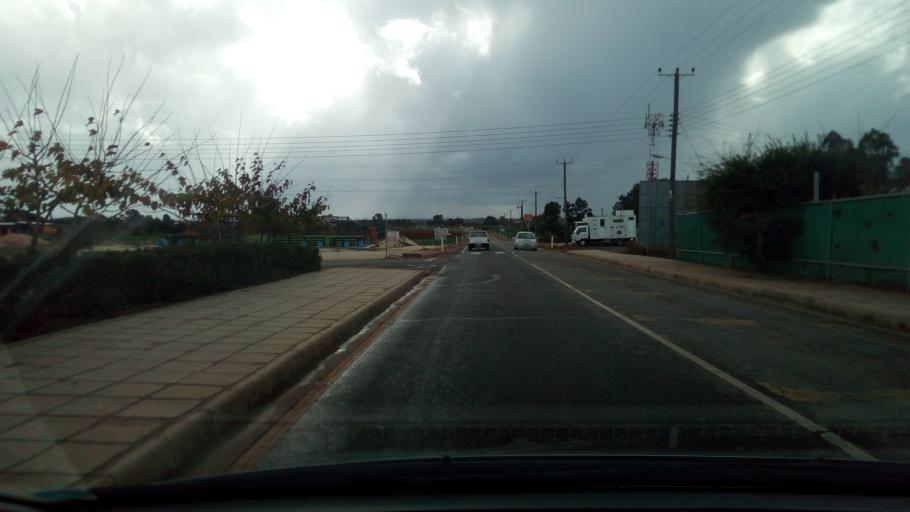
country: CY
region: Ammochostos
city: Liopetri
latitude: 35.0003
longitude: 33.8926
